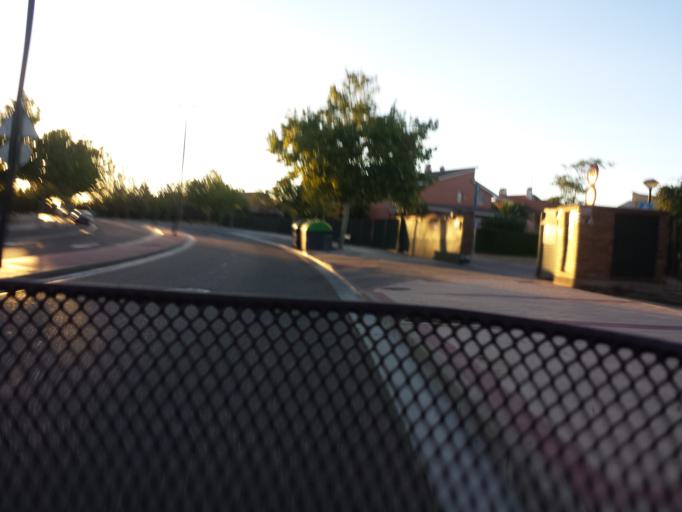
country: ES
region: Aragon
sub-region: Provincia de Zaragoza
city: Montecanal
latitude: 41.6311
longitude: -0.9371
